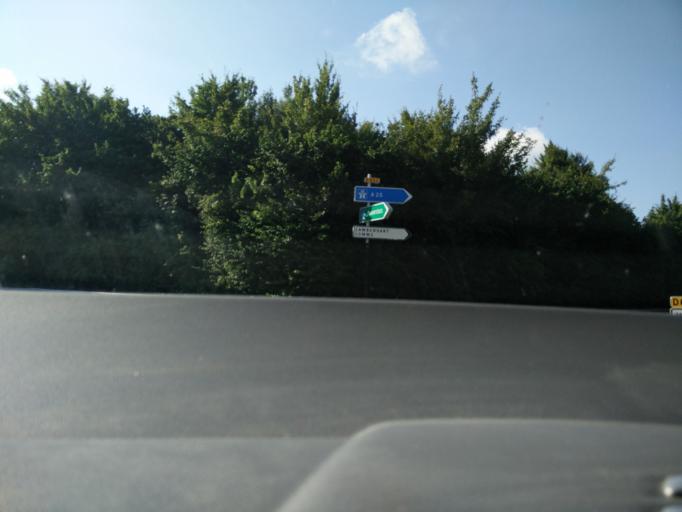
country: FR
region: Nord-Pas-de-Calais
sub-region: Departement du Nord
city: Wambrechies
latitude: 50.6792
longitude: 3.0509
